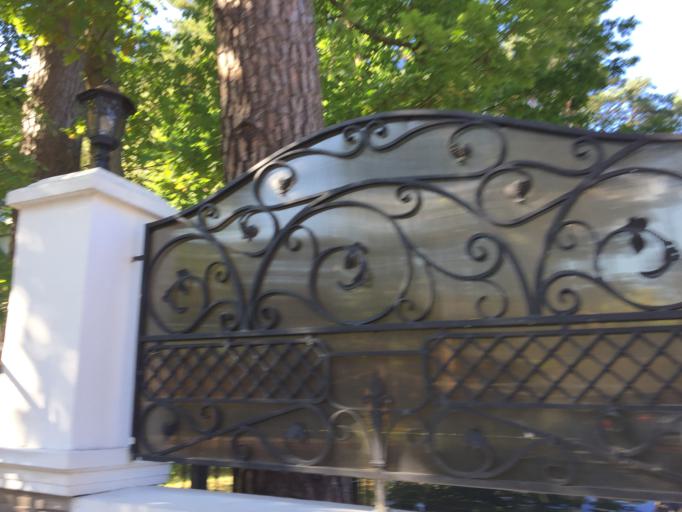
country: RU
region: Kaliningrad
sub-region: Gorod Svetlogorsk
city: Svetlogorsk
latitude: 54.9432
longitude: 20.1633
